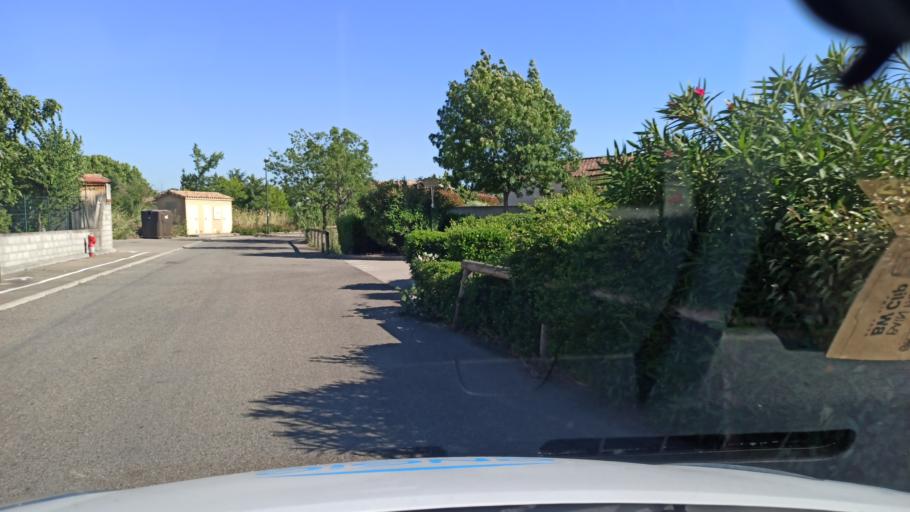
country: FR
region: Provence-Alpes-Cote d'Azur
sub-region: Departement du Vaucluse
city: Morieres-les-Avignon
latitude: 43.9560
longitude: 4.8968
